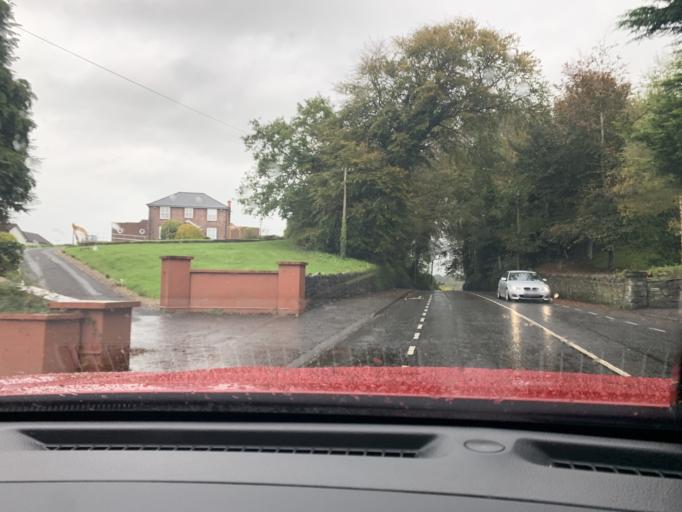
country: IE
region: Connaught
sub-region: Sligo
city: Sligo
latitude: 54.2744
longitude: -8.4610
